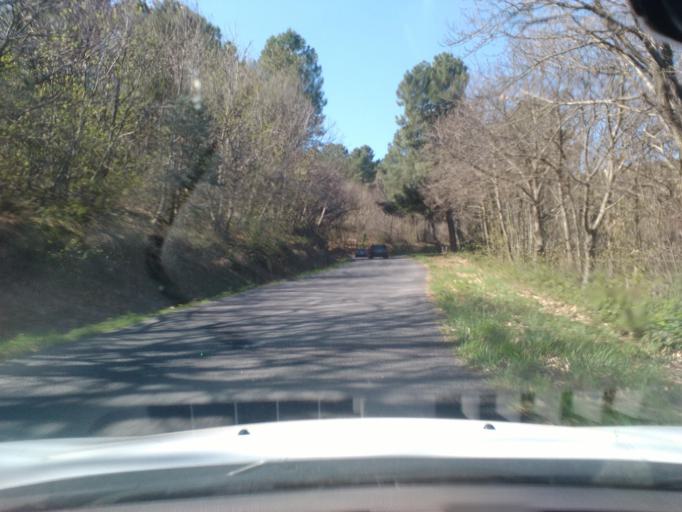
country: FR
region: Languedoc-Roussillon
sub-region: Departement du Gard
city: Valleraugue
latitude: 44.1631
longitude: 3.7497
